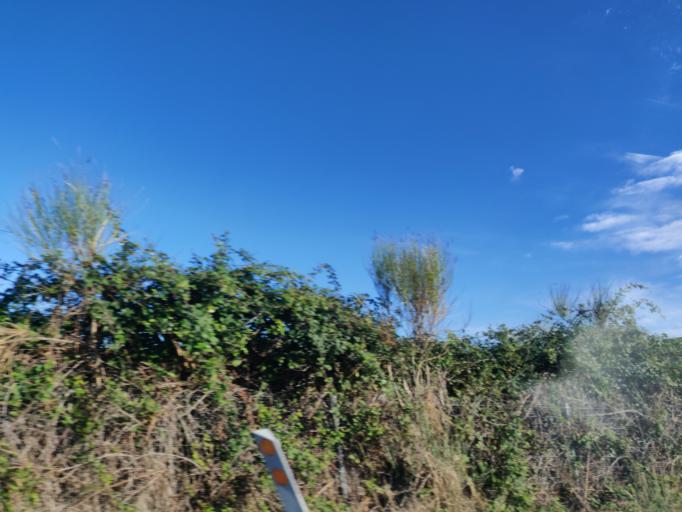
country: IT
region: Tuscany
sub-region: Provincia di Grosseto
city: Scarlino Scalo
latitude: 42.9602
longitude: 10.8297
